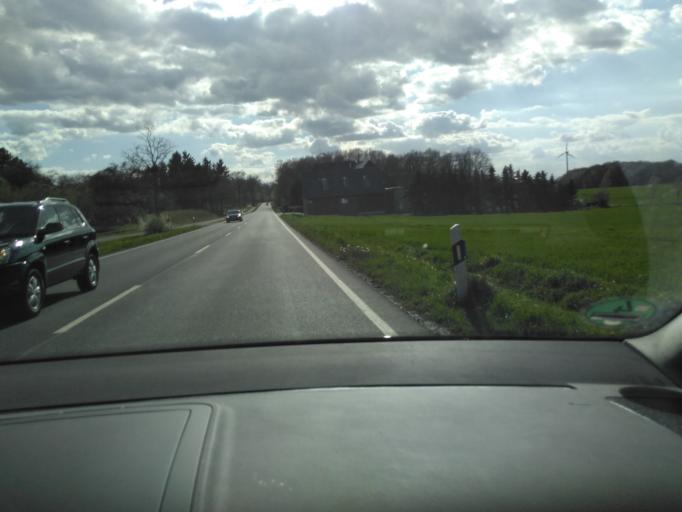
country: DE
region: North Rhine-Westphalia
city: Oelde
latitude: 51.7778
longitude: 8.1239
